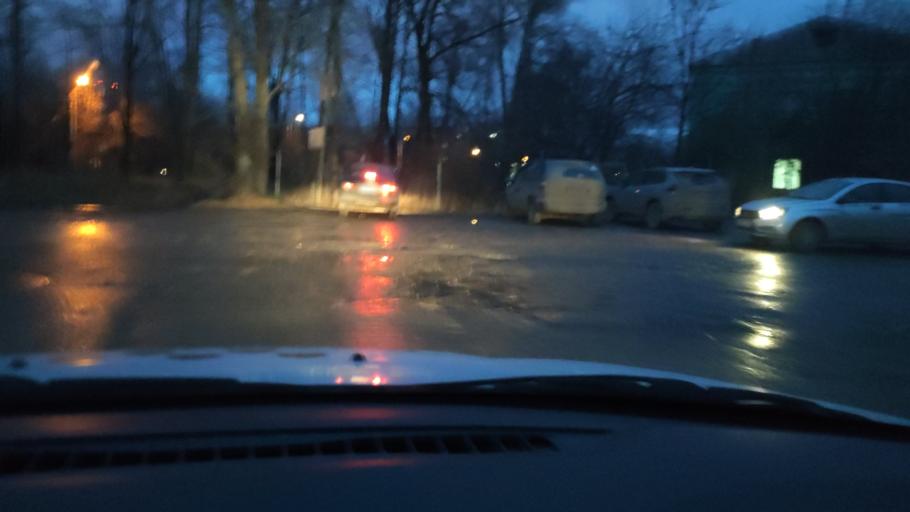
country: RU
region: Perm
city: Perm
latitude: 57.9744
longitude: 56.2787
